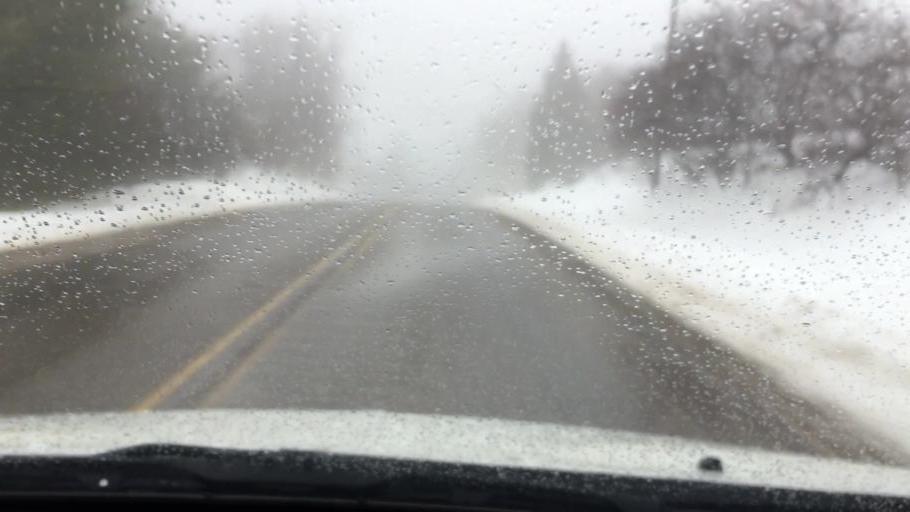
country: US
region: Michigan
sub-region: Charlevoix County
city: East Jordan
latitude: 45.1242
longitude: -85.1801
